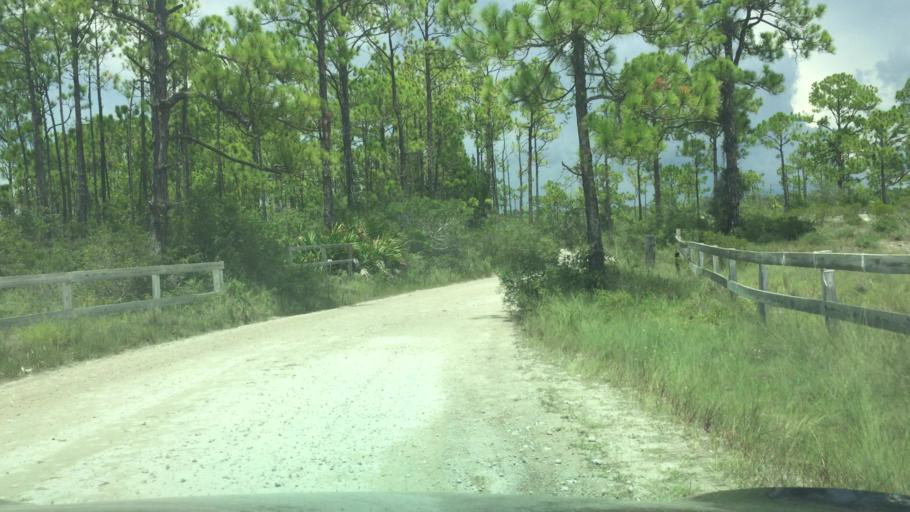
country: US
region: Florida
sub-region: Bay County
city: Mexico Beach
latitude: 29.9601
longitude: -85.4570
